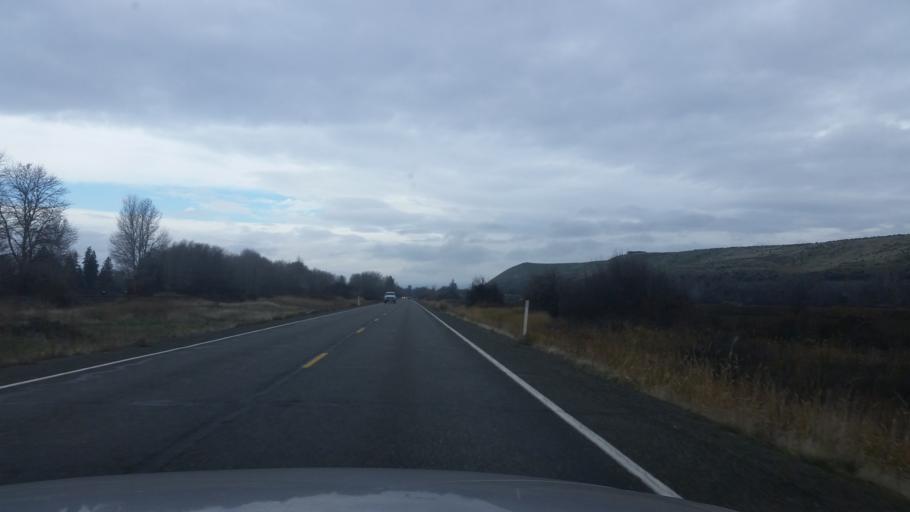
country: US
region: Washington
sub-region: Kittitas County
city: Ellensburg
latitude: 47.0460
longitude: -120.6275
